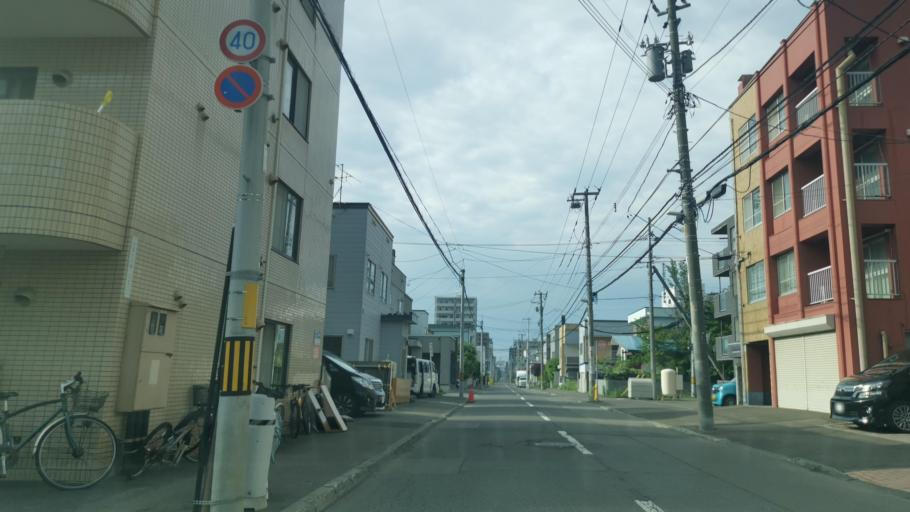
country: JP
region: Hokkaido
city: Sapporo
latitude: 43.0386
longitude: 141.3384
